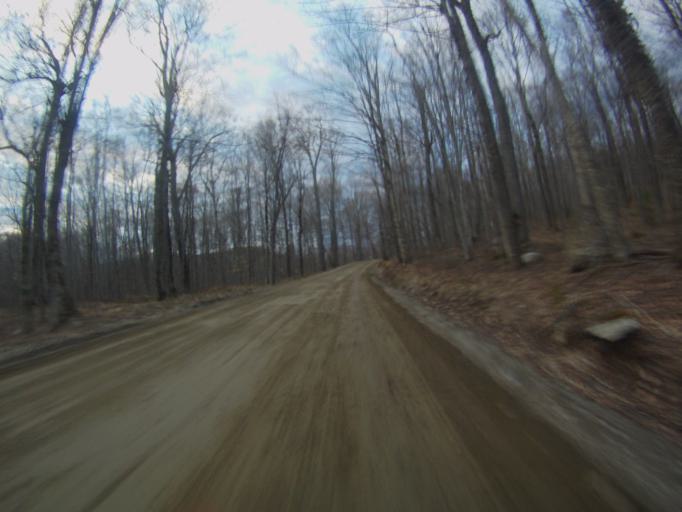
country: US
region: Vermont
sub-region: Rutland County
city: Brandon
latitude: 43.9295
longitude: -73.0205
